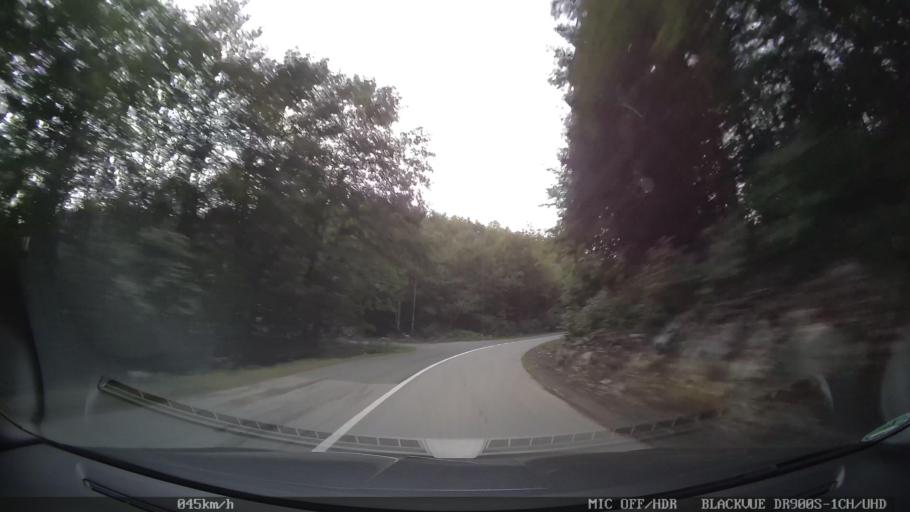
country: HR
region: Primorsko-Goranska
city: Novi Vinodolski
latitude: 45.1954
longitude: 14.8892
